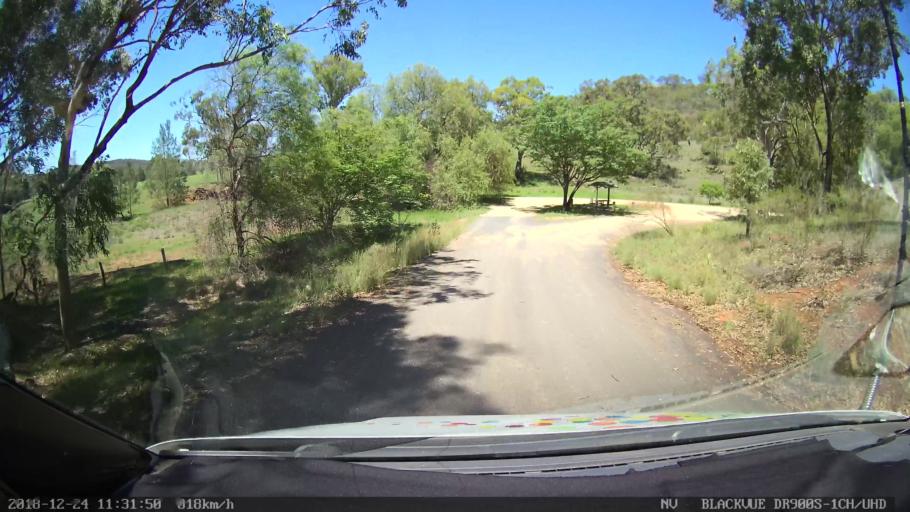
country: AU
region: New South Wales
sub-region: Upper Hunter Shire
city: Merriwa
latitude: -32.2140
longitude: 150.4602
